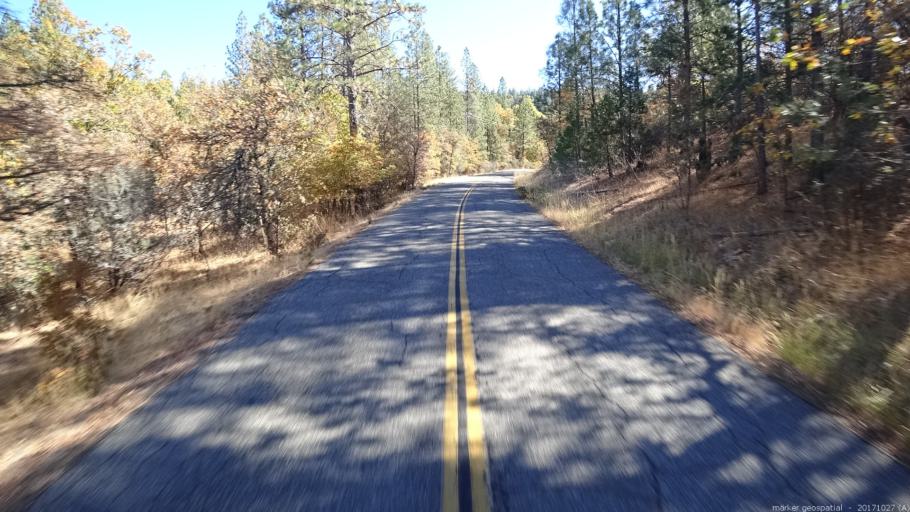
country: US
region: California
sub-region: Shasta County
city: Shingletown
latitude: 40.7258
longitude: -121.9698
